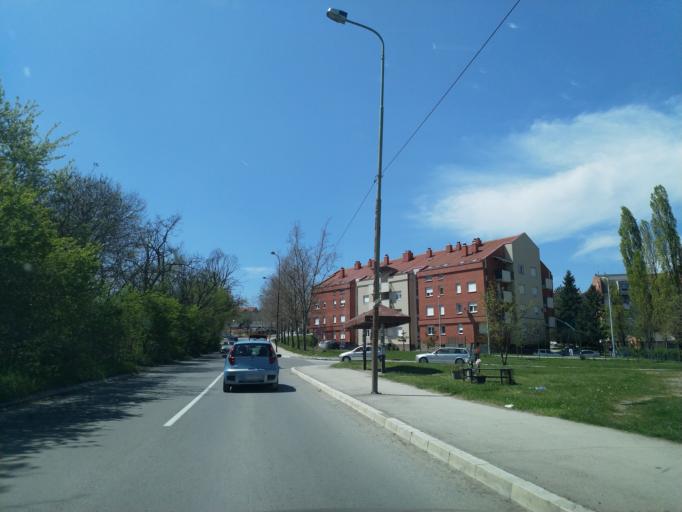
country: RS
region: Central Serbia
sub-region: Belgrade
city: Lazarevac
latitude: 44.3767
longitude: 20.2509
